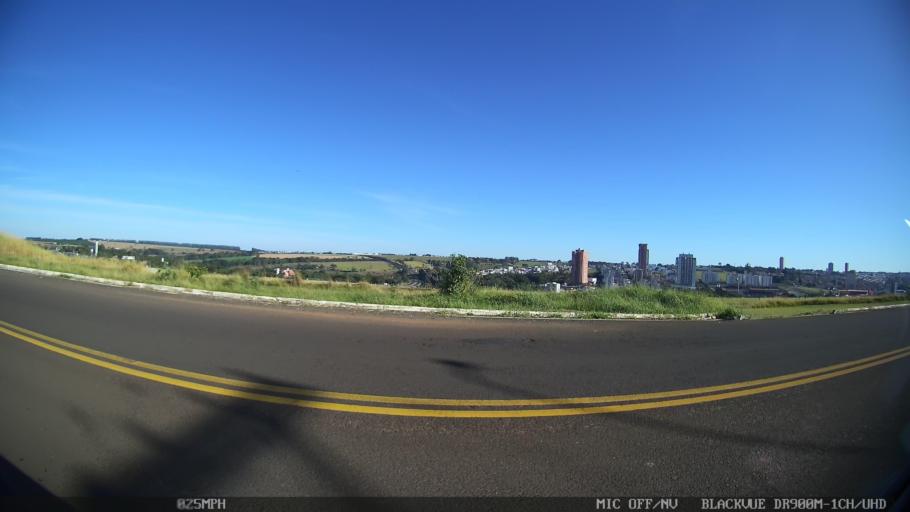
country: BR
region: Sao Paulo
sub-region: Franca
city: Franca
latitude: -20.5606
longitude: -47.4095
